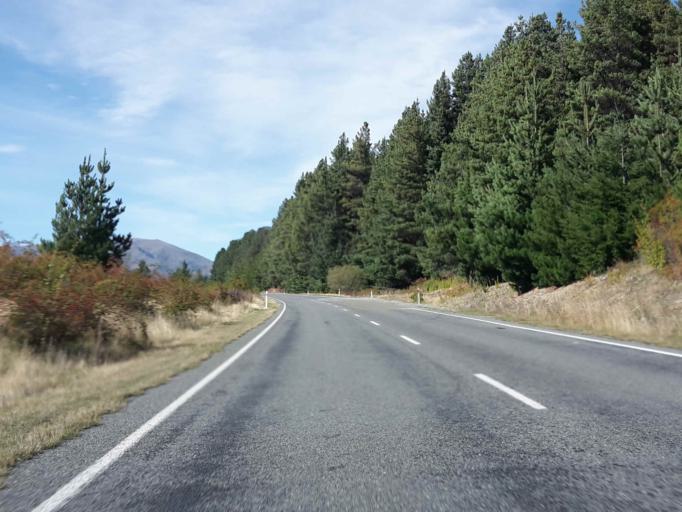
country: NZ
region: Otago
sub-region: Queenstown-Lakes District
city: Wanaka
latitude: -44.5128
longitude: 169.7953
